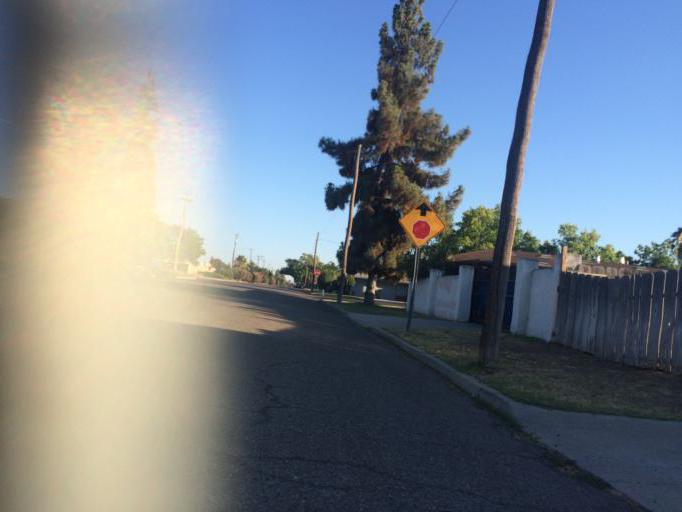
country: US
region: California
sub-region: Fresno County
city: Tarpey Village
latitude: 36.7785
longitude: -119.7318
